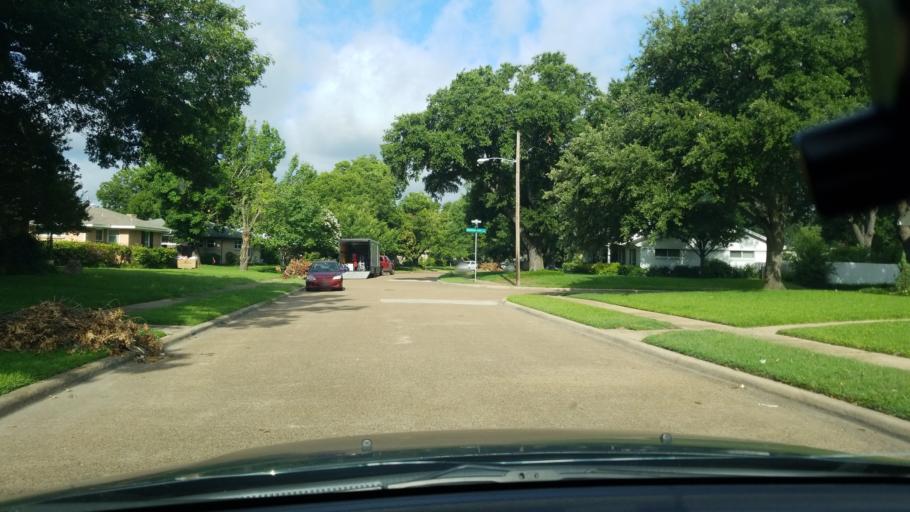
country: US
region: Texas
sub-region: Dallas County
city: Mesquite
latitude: 32.8189
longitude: -96.6869
